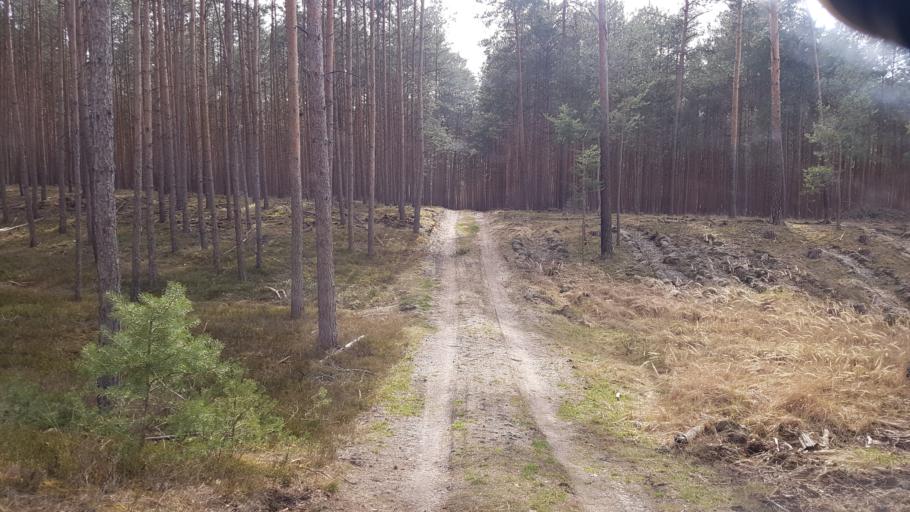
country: DE
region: Brandenburg
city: Schlieben
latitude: 51.6851
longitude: 13.4385
